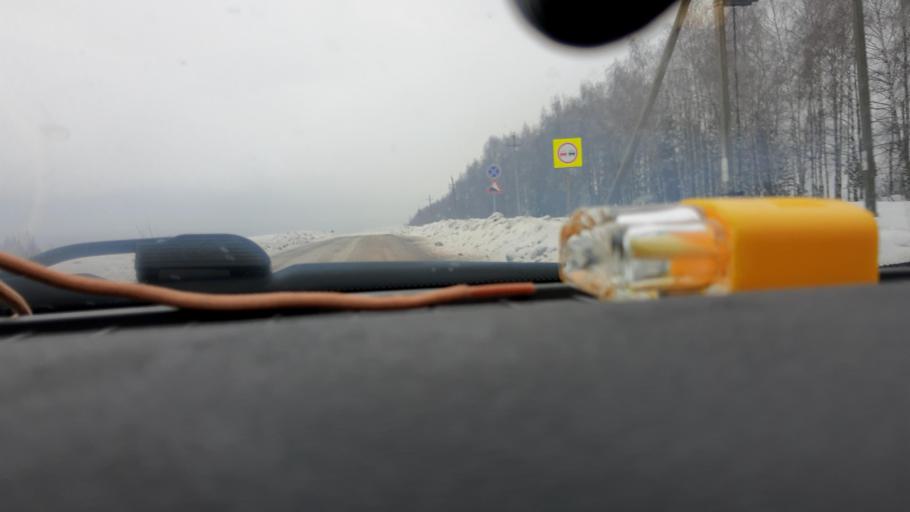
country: RU
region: Bashkortostan
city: Iglino
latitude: 54.6579
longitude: 56.4247
